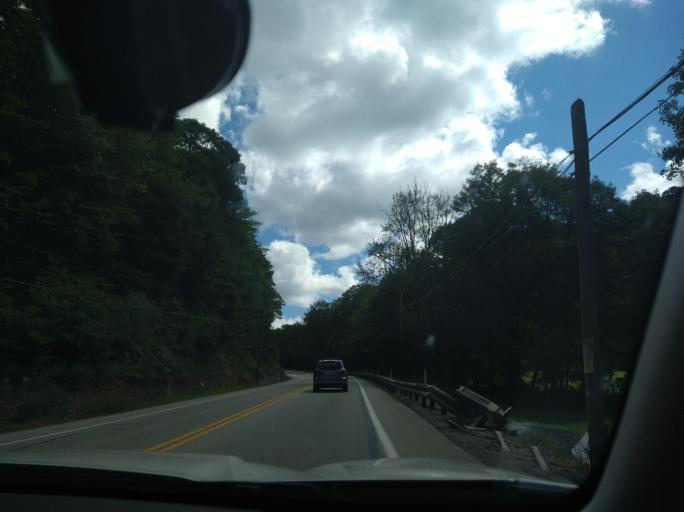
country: US
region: Pennsylvania
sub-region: Fayette County
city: Bear Rocks
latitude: 40.0706
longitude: -79.2908
